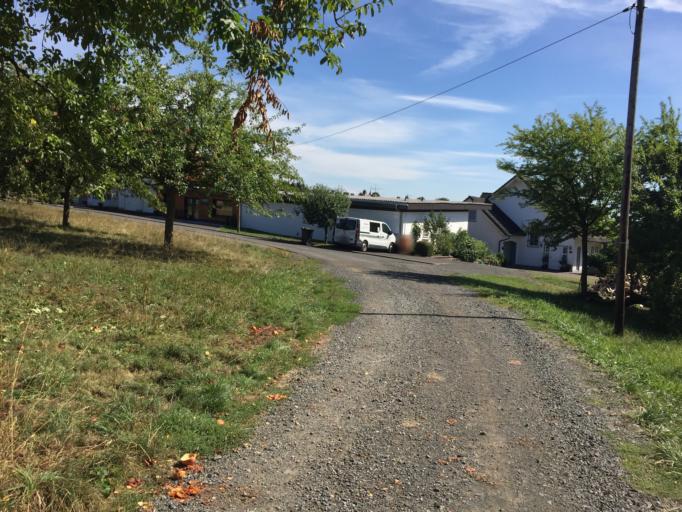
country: DE
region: Hesse
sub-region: Regierungsbezirk Giessen
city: Reiskirchen
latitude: 50.5952
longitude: 8.8767
